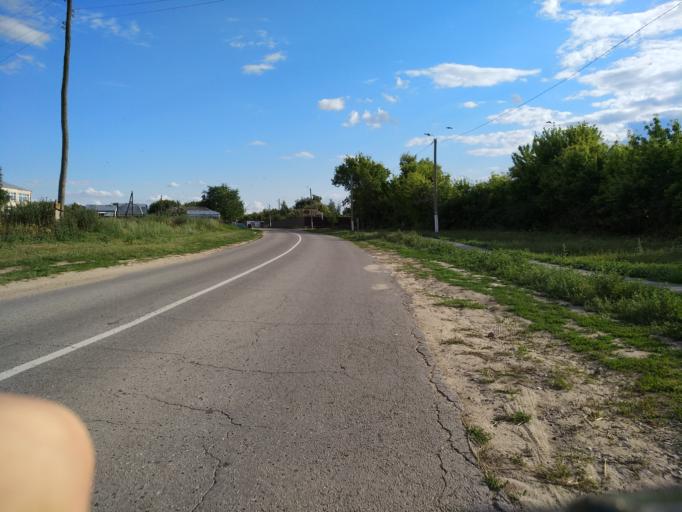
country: RU
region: Lipetsk
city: Dobrinka
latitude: 52.0392
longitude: 40.5537
